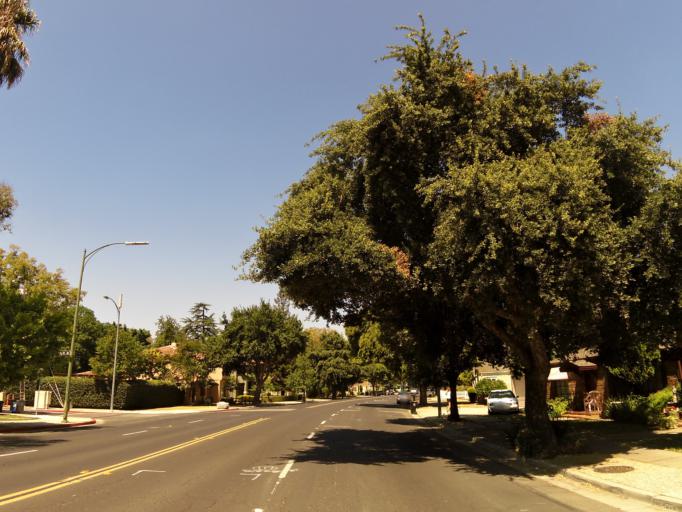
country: US
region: California
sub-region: Santa Clara County
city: Buena Vista
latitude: 37.2966
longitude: -121.8925
